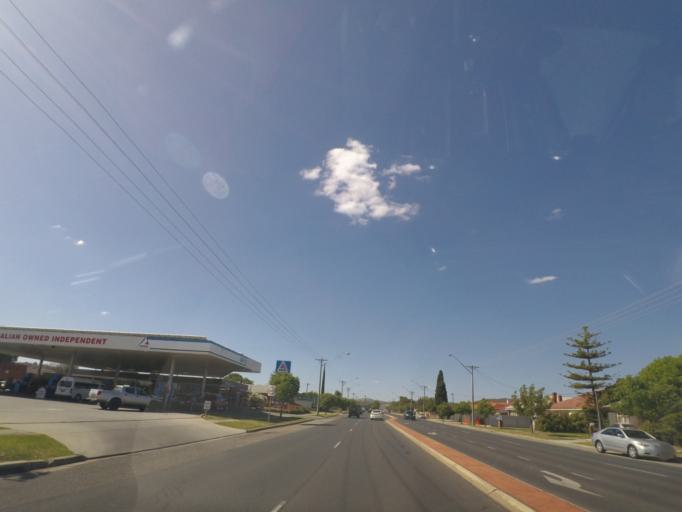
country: AU
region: New South Wales
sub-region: Albury Municipality
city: North Albury
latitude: -36.0577
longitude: 146.9326
